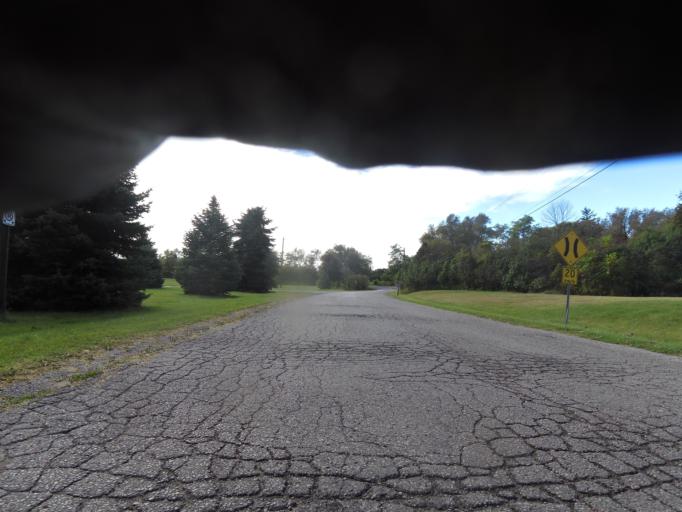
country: CA
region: Ontario
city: Cobourg
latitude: 43.9438
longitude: -78.3229
